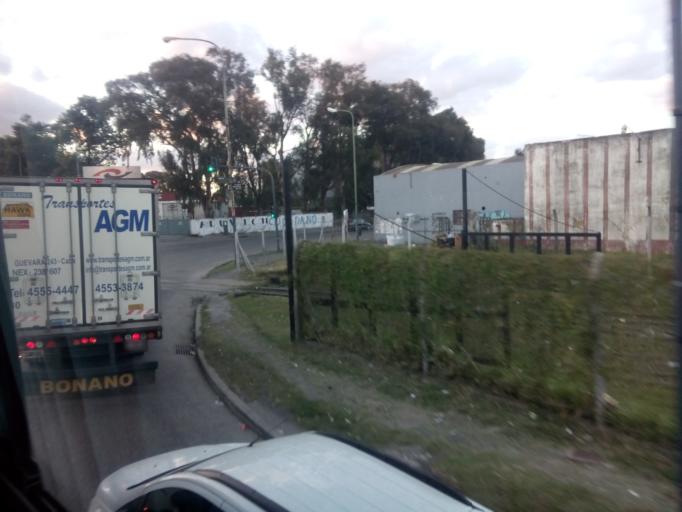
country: AR
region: Buenos Aires F.D.
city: Retiro
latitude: -34.5781
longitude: -58.3846
